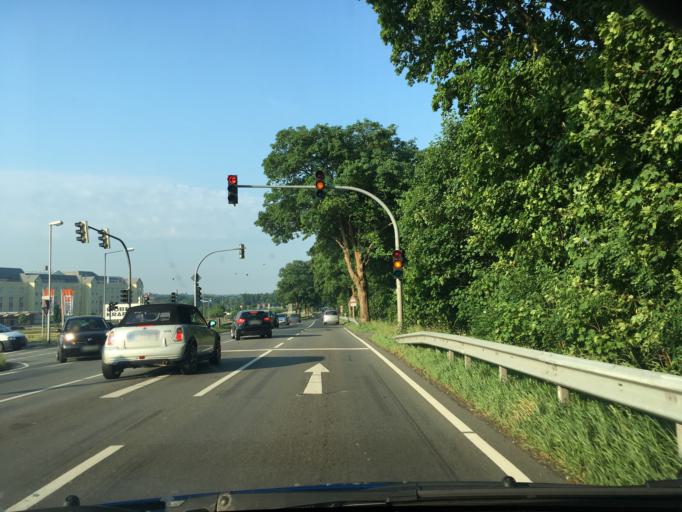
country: DE
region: Lower Saxony
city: Buchholz in der Nordheide
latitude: 53.3538
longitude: 9.8614
